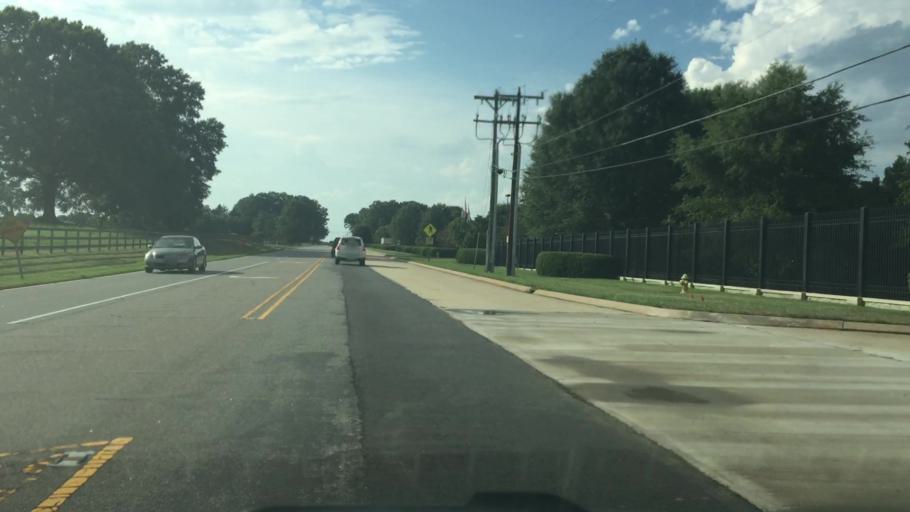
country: US
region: North Carolina
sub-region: Iredell County
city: Mooresville
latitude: 35.5425
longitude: -80.7688
